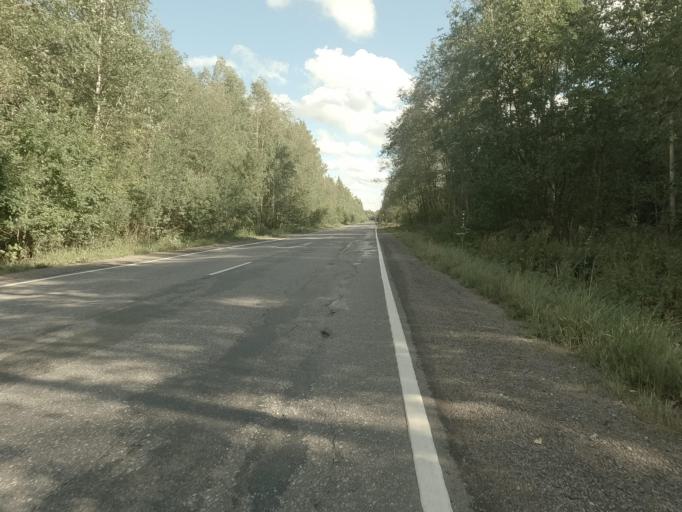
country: RU
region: Leningrad
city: Shcheglovo
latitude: 59.9929
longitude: 30.8807
